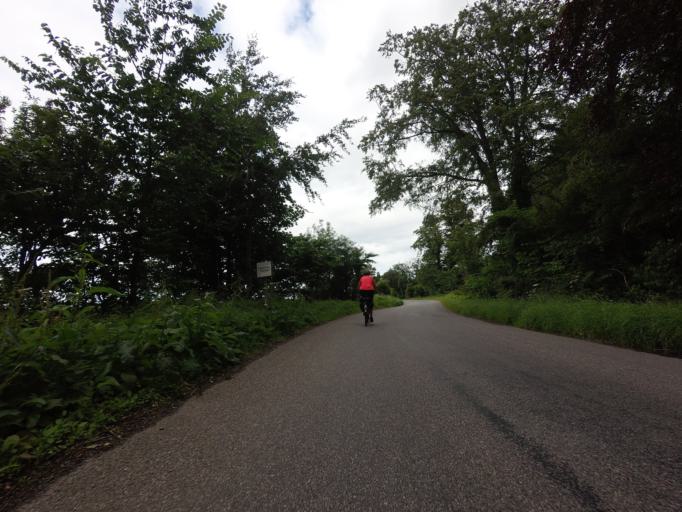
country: GB
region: Scotland
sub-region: Moray
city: Forres
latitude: 57.6193
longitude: -3.6520
